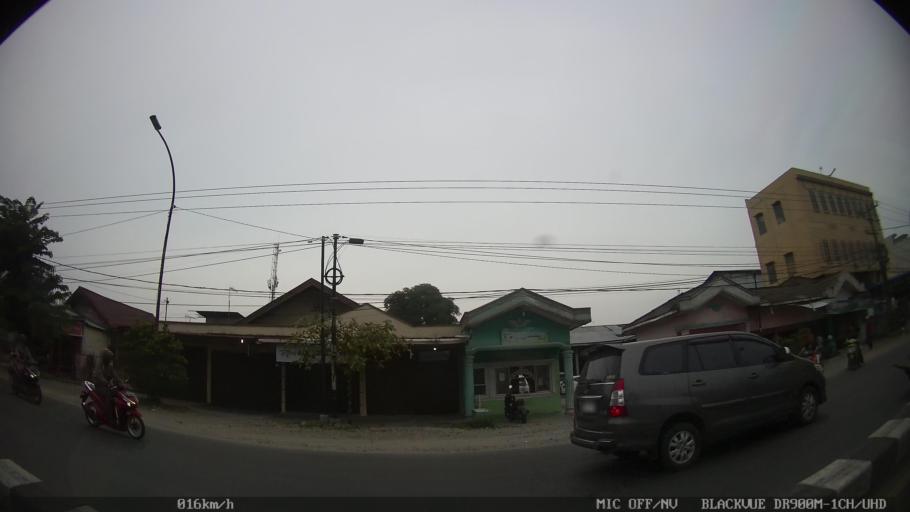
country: ID
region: North Sumatra
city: Medan
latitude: 3.5971
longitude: 98.7137
